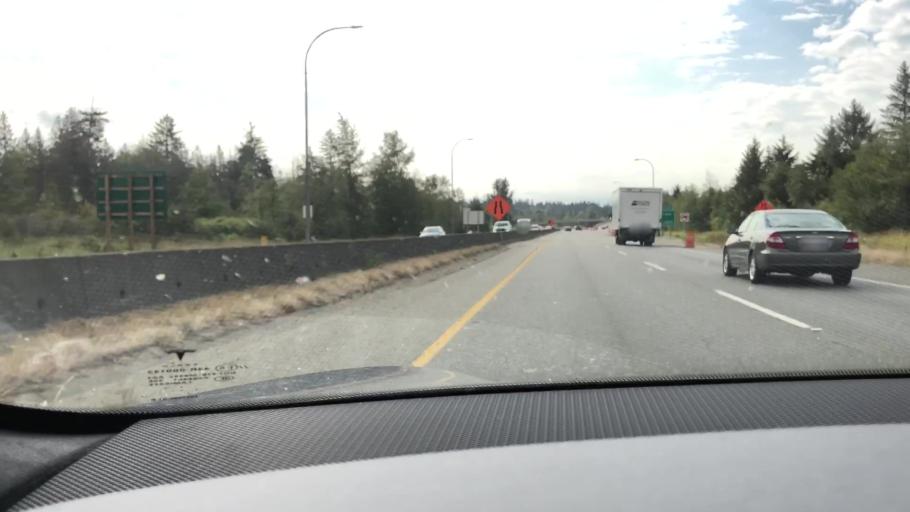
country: CA
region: British Columbia
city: Delta
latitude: 49.1392
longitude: -122.9336
